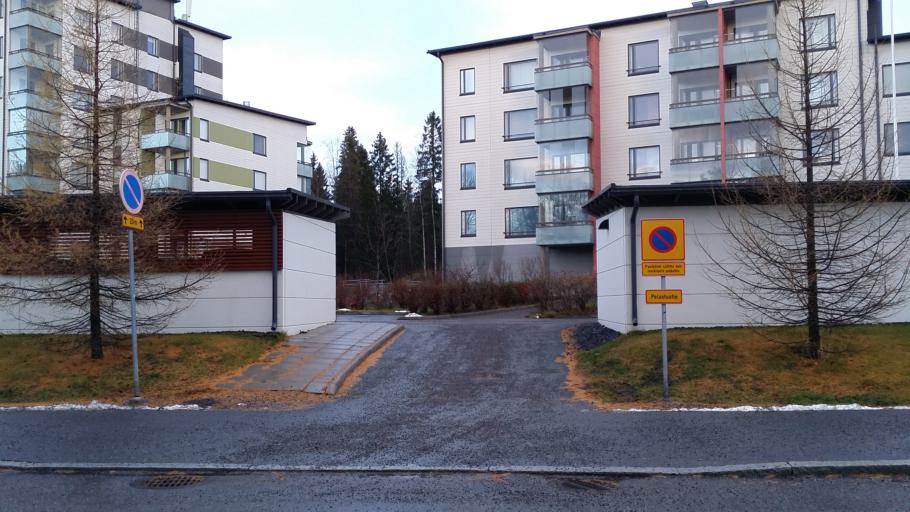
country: FI
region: Pirkanmaa
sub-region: Tampere
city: Pirkkala
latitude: 61.5064
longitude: 23.6390
